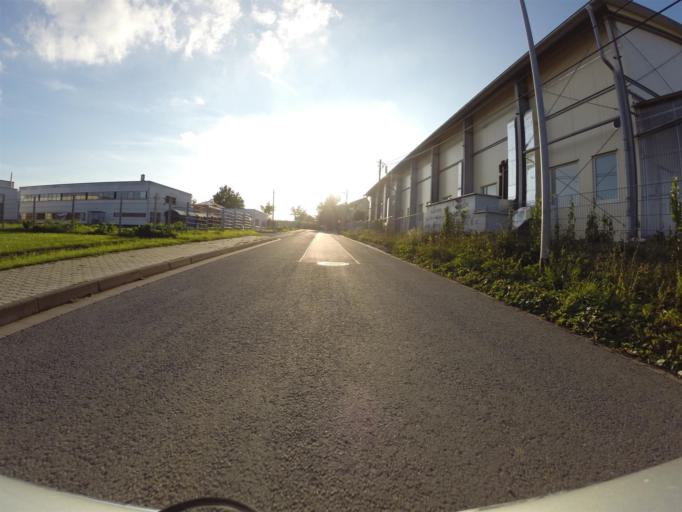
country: DE
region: Thuringia
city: Bucha
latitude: 50.8778
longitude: 11.5120
